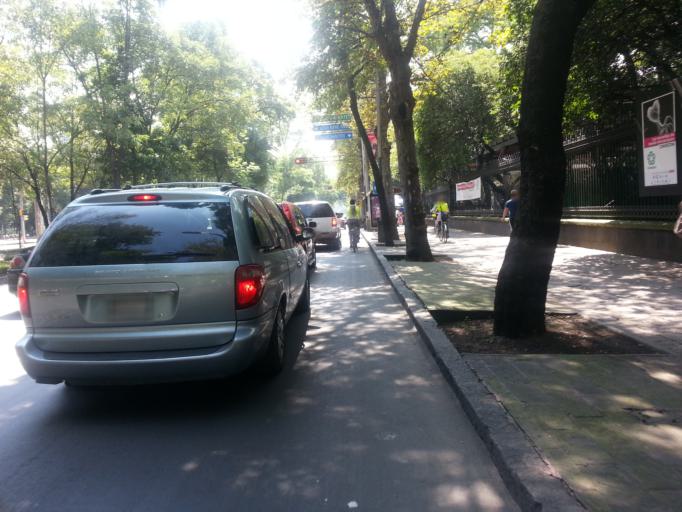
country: MX
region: Mexico City
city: Polanco
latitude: 19.4240
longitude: -99.1813
